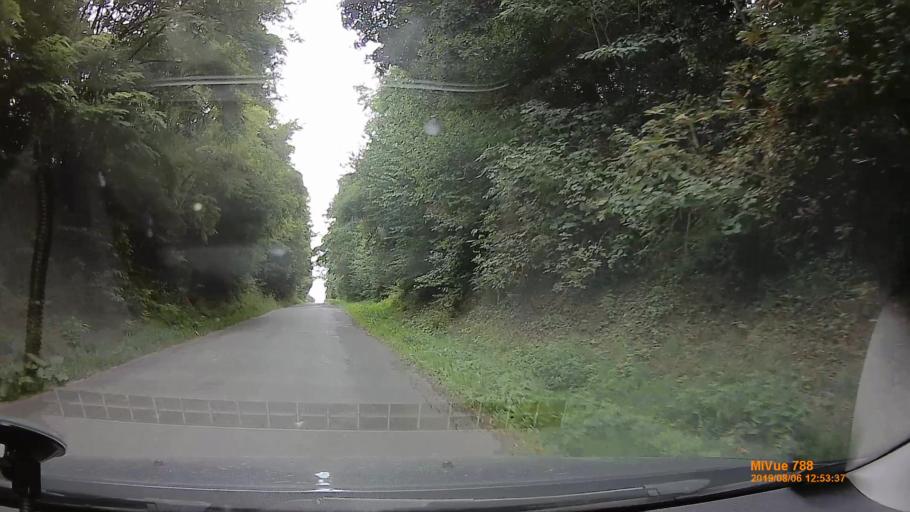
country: HU
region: Zala
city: Pacsa
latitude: 46.6377
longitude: 17.0042
